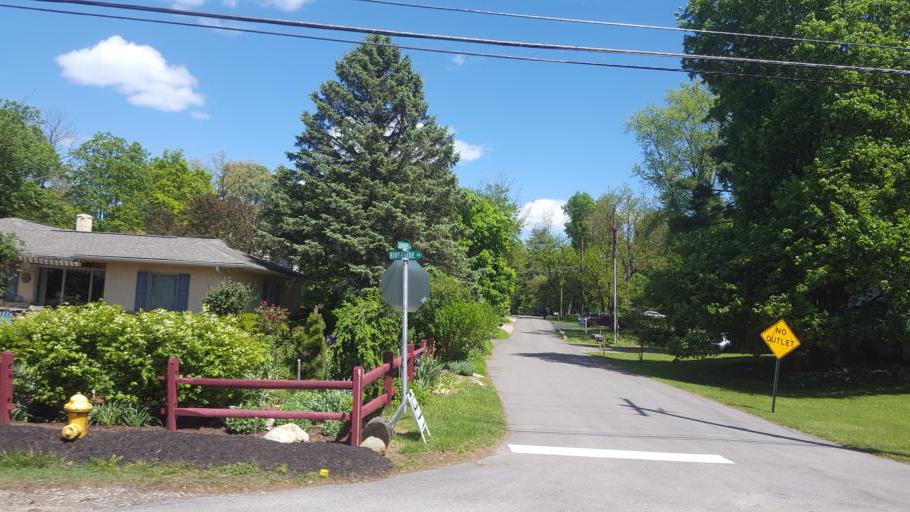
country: US
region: Ohio
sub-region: Franklin County
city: Upper Arlington
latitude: 40.0351
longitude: -83.0930
